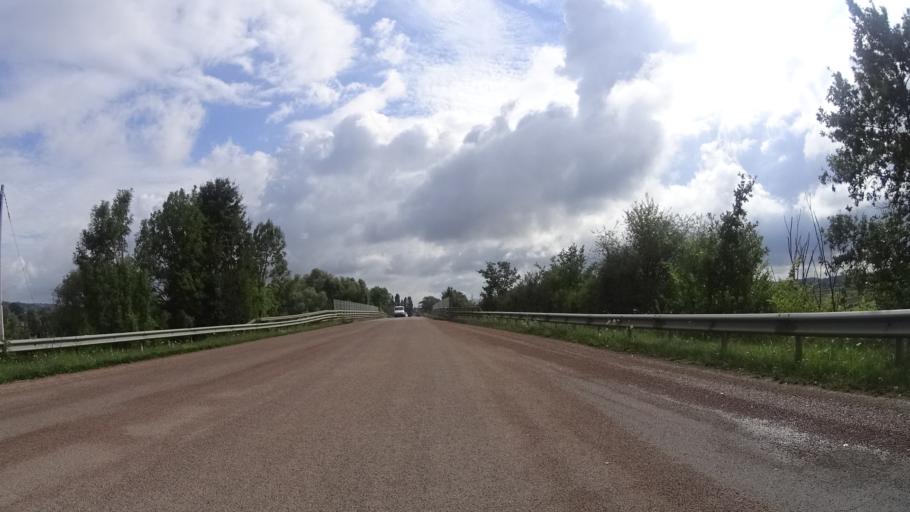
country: FR
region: Bourgogne
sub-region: Departement de l'Yonne
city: Vergigny
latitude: 47.9685
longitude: 3.7038
